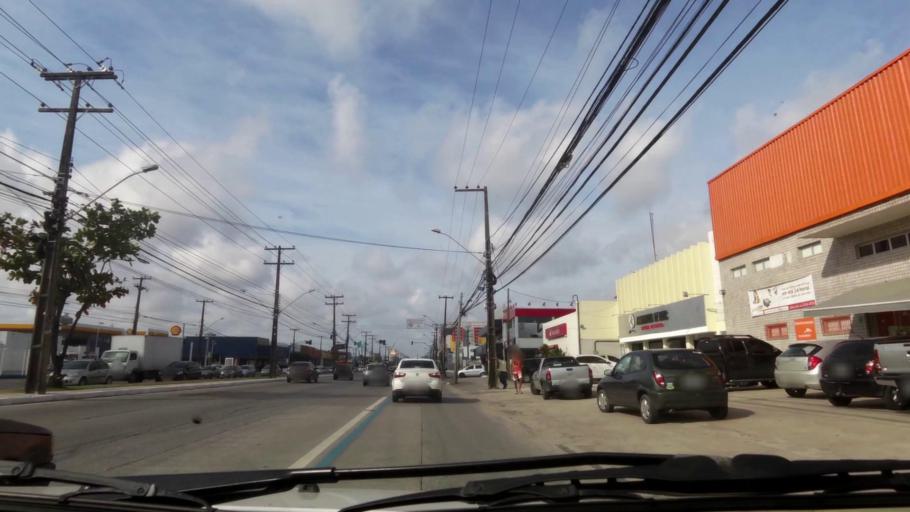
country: BR
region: Pernambuco
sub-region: Recife
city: Recife
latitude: -8.1071
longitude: -34.9116
